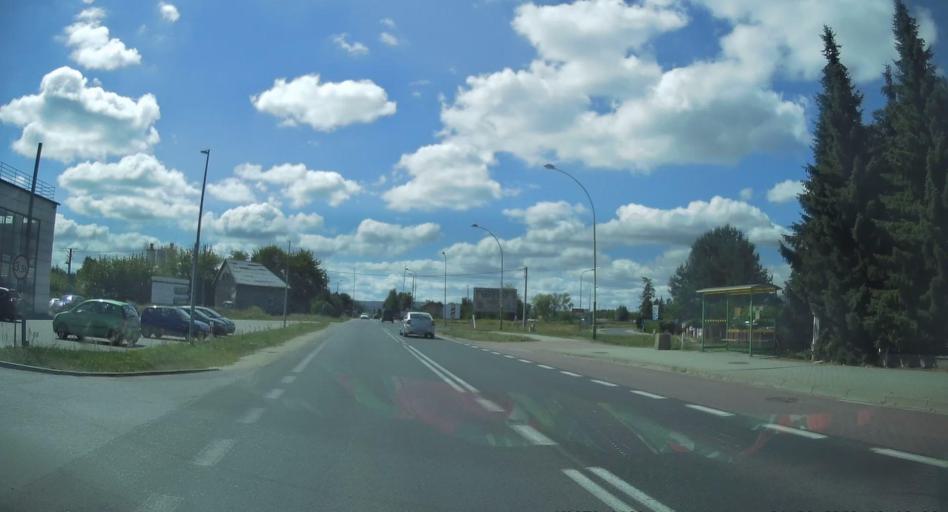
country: PL
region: Subcarpathian Voivodeship
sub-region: Powiat debicki
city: Brzeznica
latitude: 50.0716
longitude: 21.4497
